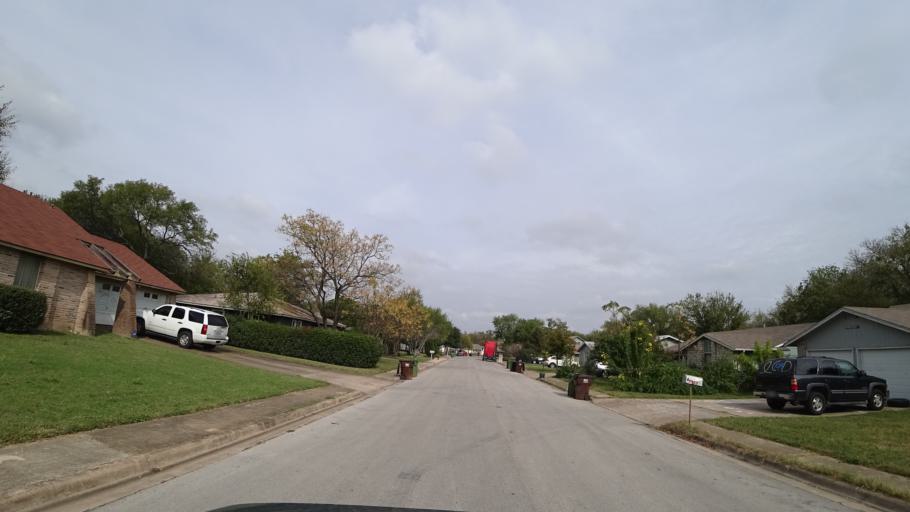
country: US
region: Texas
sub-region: Williamson County
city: Round Rock
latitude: 30.4943
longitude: -97.6841
